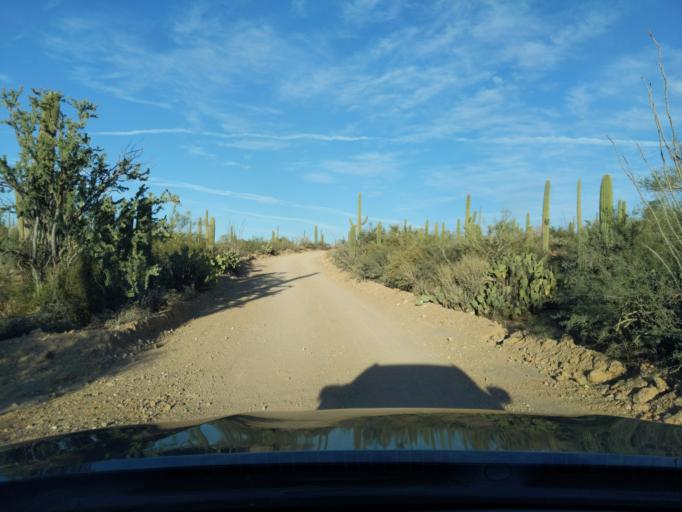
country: US
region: Arizona
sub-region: Pima County
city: Picture Rocks
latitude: 32.2812
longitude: -111.1917
